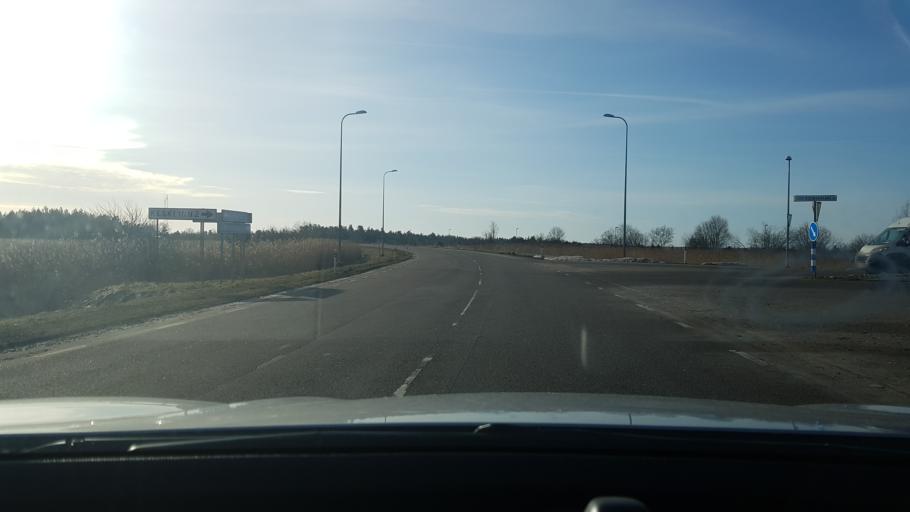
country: EE
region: Saare
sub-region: Kuressaare linn
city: Kuressaare
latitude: 58.2371
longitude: 22.5003
